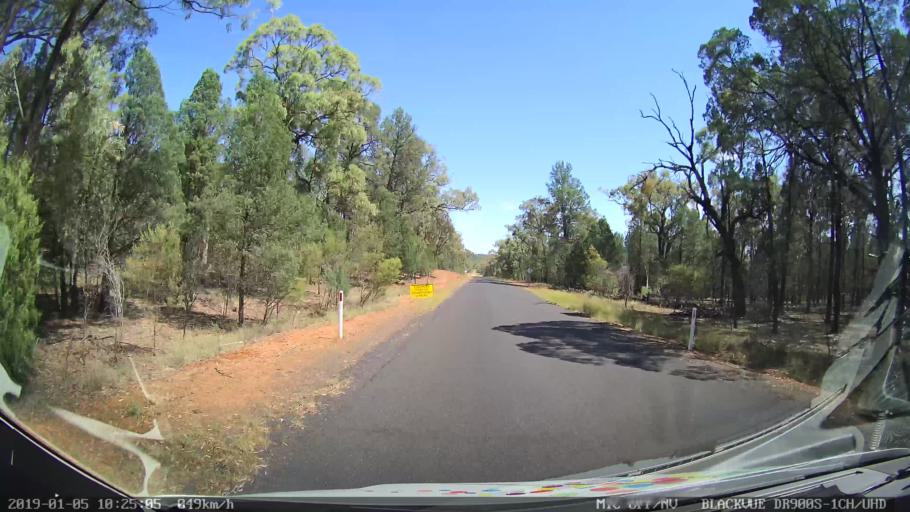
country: AU
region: New South Wales
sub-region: Gilgandra
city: Gilgandra
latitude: -31.5640
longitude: 148.9612
